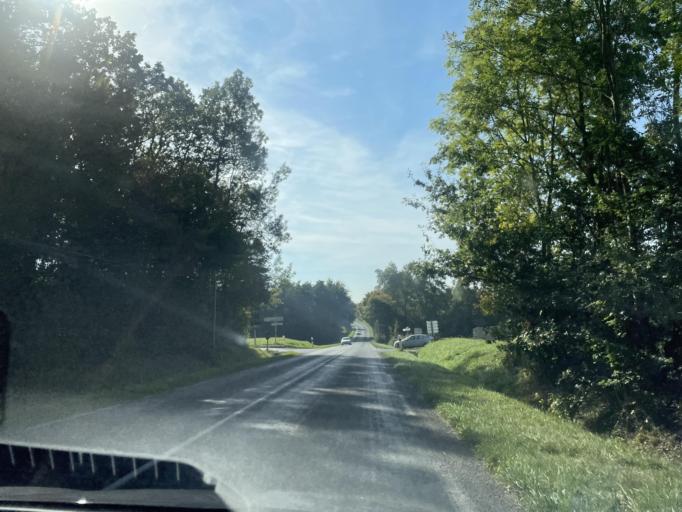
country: FR
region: Ile-de-France
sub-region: Departement de Seine-et-Marne
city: Coulommiers
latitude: 48.8440
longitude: 3.0884
